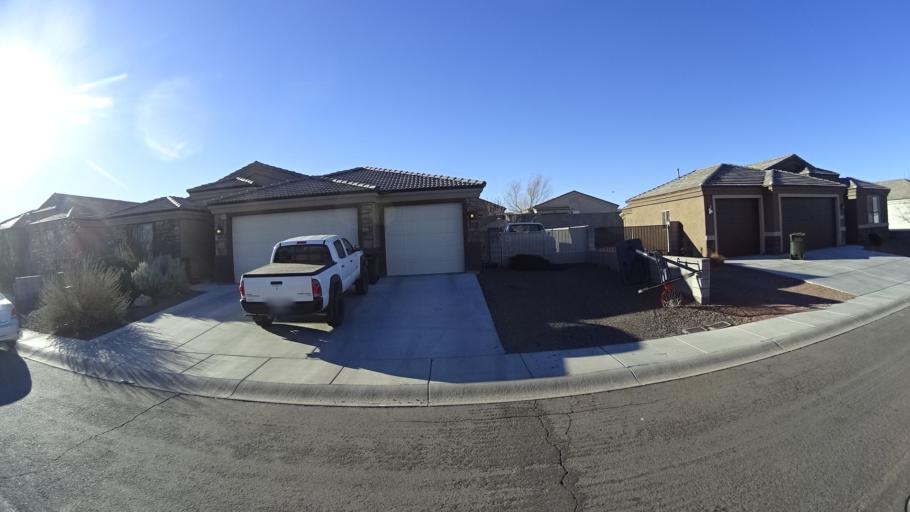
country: US
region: Arizona
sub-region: Mohave County
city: Kingman
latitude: 35.1930
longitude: -114.0014
